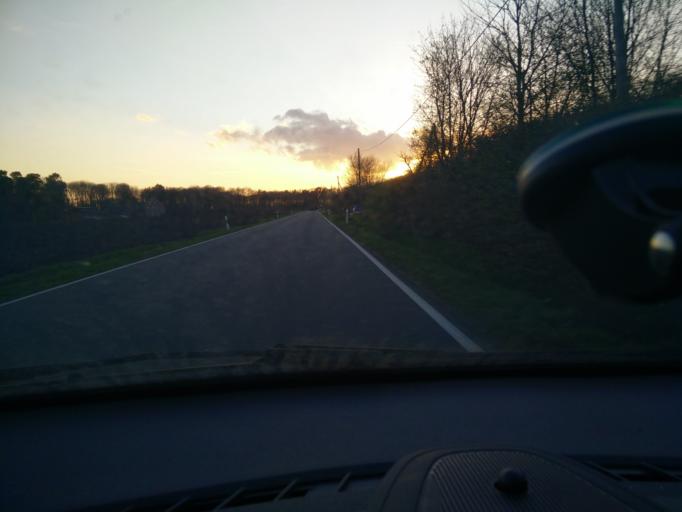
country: DE
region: North Rhine-Westphalia
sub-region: Regierungsbezirk Munster
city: Raesfeld
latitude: 51.7806
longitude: 6.8820
